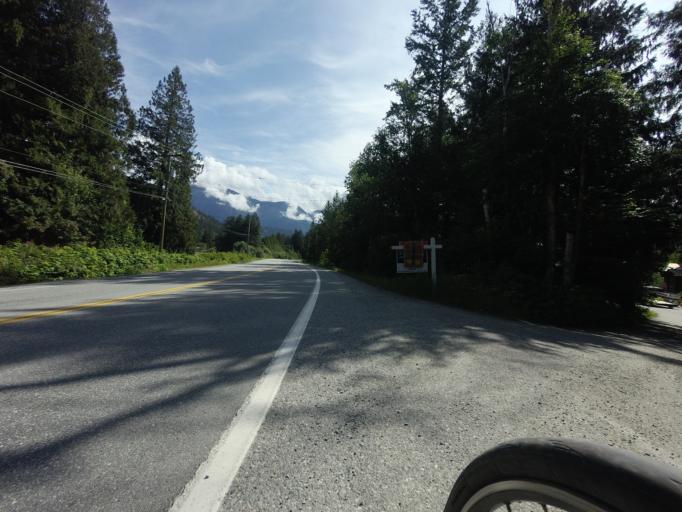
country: CA
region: British Columbia
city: Pemberton
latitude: 50.3088
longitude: -122.7415
